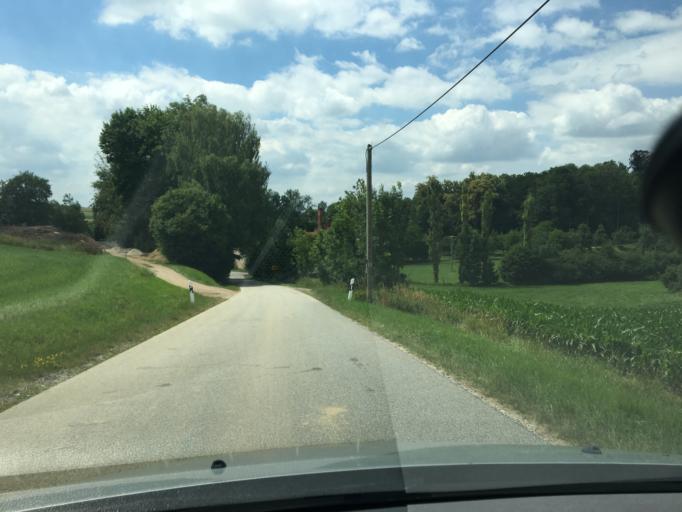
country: DE
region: Bavaria
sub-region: Upper Bavaria
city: Egglkofen
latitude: 48.3952
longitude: 12.4556
